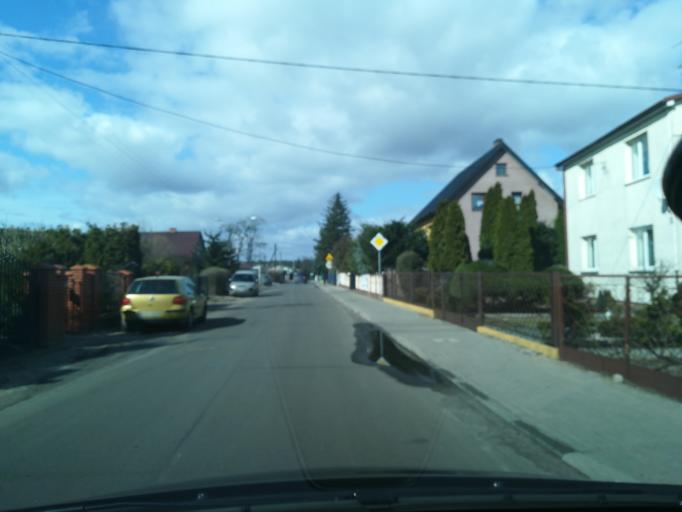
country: PL
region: Kujawsko-Pomorskie
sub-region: Powiat aleksandrowski
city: Ciechocinek
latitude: 52.8676
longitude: 18.7499
